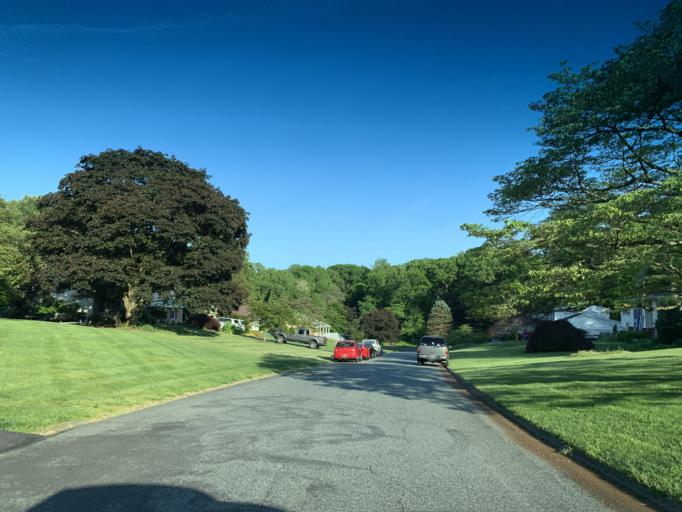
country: US
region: Maryland
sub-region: Harford County
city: Bel Air South
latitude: 39.5102
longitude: -76.2925
